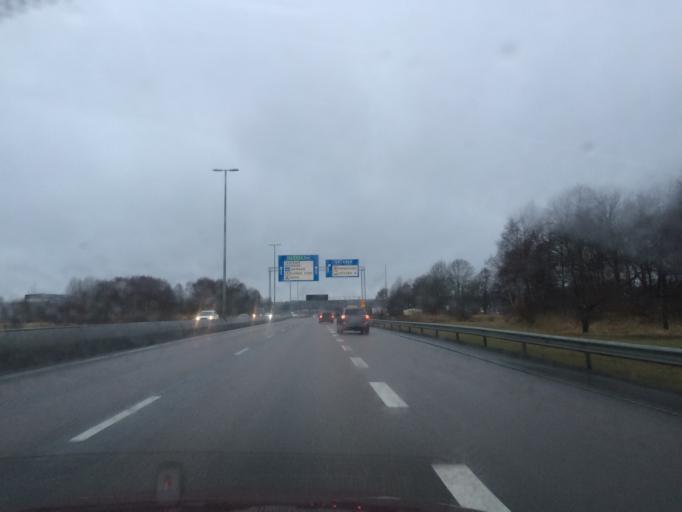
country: SE
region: Vaestra Goetaland
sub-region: Goteborg
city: Majorna
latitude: 57.6460
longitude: 11.9462
